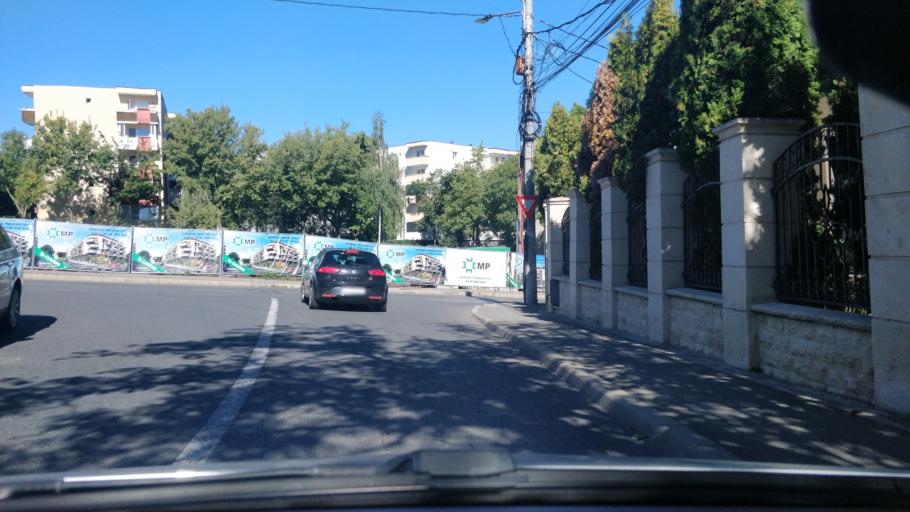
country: RO
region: Cluj
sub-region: Municipiul Cluj-Napoca
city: Cluj-Napoca
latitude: 46.7582
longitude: 23.5840
